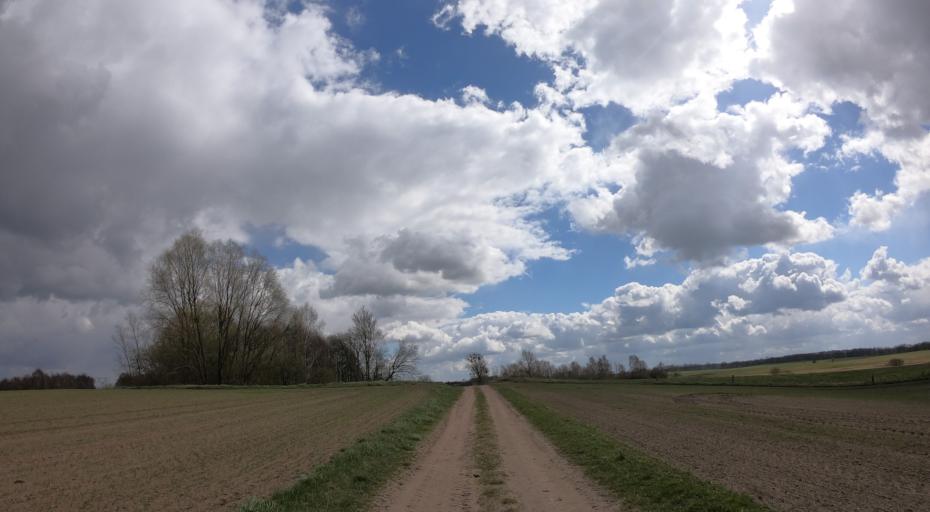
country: PL
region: West Pomeranian Voivodeship
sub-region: Powiat drawski
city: Drawsko Pomorskie
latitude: 53.5476
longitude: 15.8599
